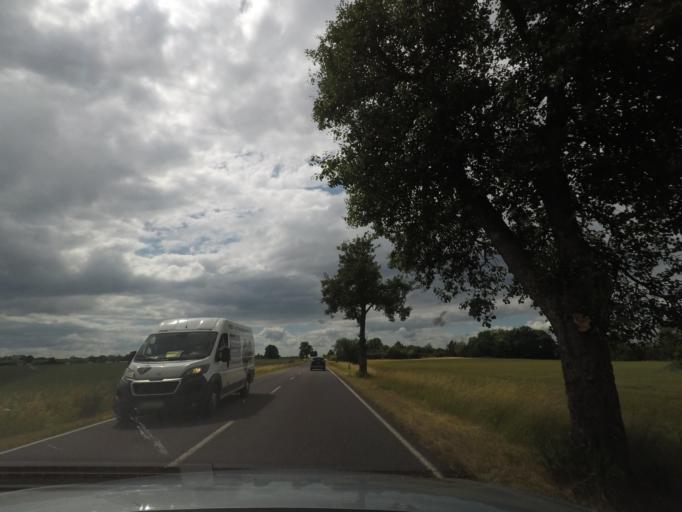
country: DE
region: Saxony-Anhalt
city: Hotensleben
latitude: 52.1049
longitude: 11.0520
